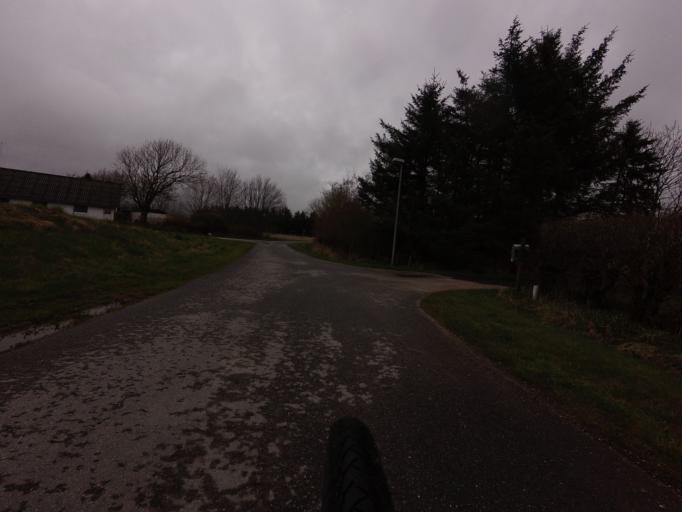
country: DK
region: North Denmark
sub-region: Jammerbugt Kommune
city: Pandrup
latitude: 57.3366
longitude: 9.7790
